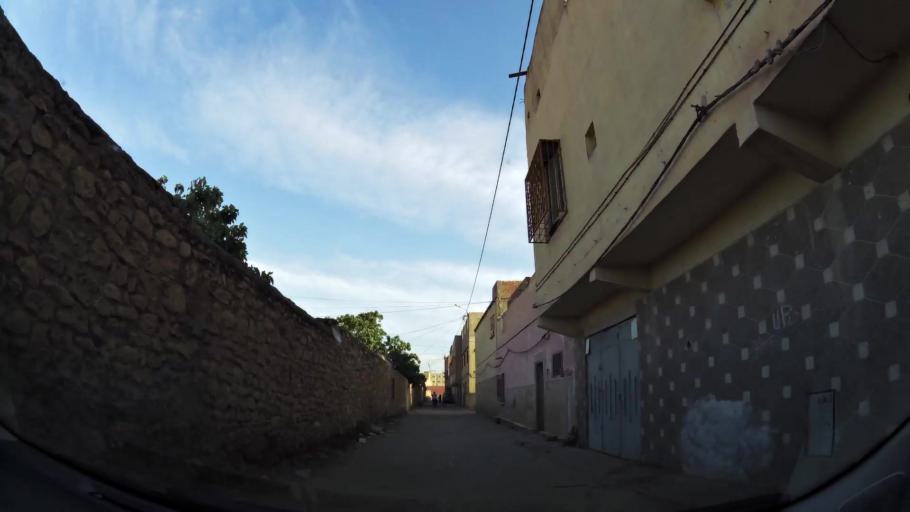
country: MA
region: Oriental
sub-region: Oujda-Angad
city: Oujda
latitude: 34.7012
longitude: -1.9048
